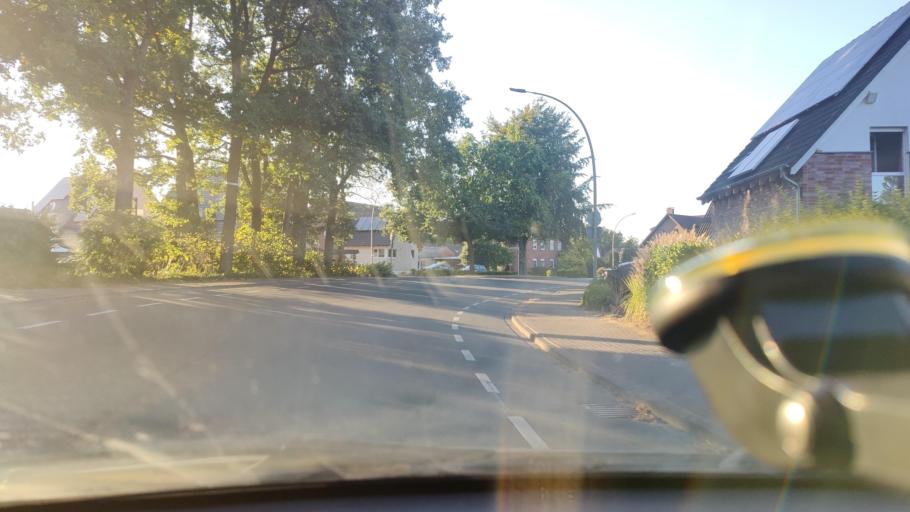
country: DE
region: North Rhine-Westphalia
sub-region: Regierungsbezirk Munster
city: Klein Reken
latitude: 51.8059
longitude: 7.0440
